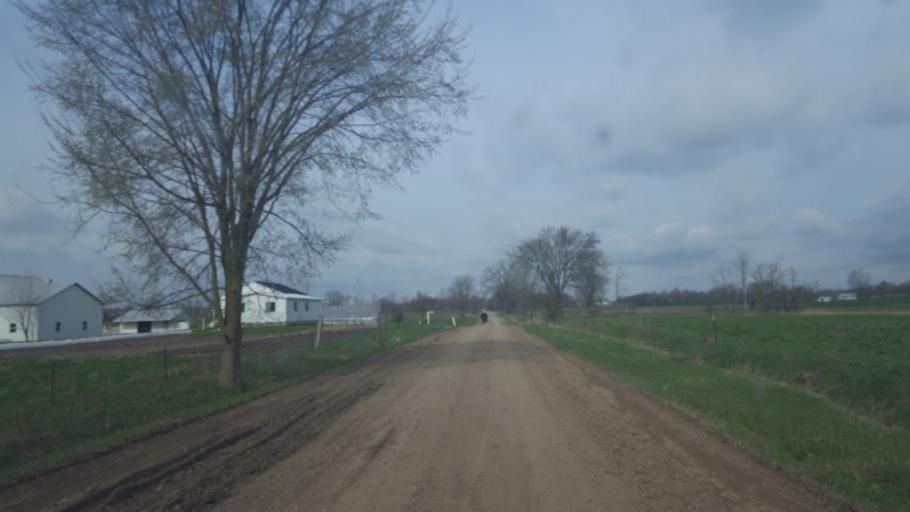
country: US
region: Michigan
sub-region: Montcalm County
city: Edmore
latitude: 43.4809
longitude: -84.9498
